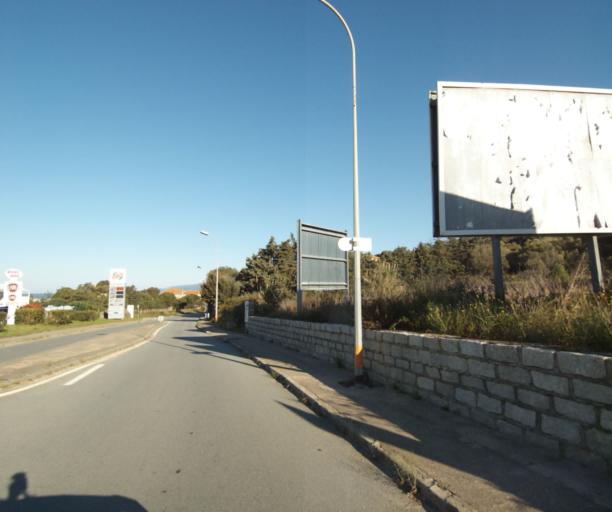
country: FR
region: Corsica
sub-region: Departement de la Corse-du-Sud
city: Propriano
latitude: 41.6722
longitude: 8.9095
